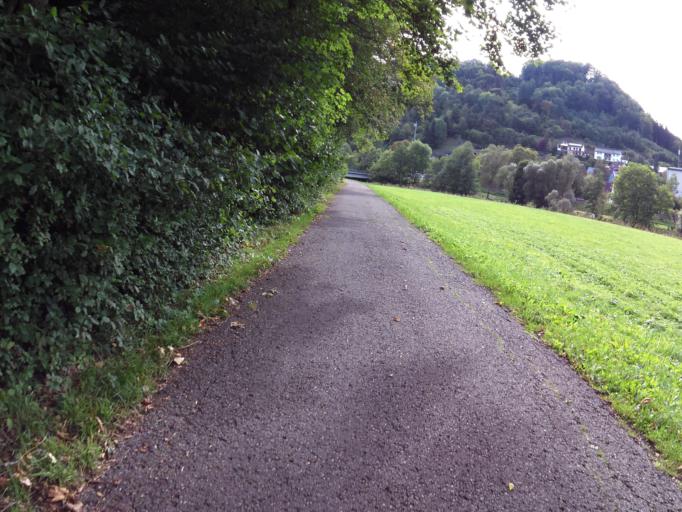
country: DE
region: Baden-Wuerttemberg
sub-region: Freiburg Region
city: Epfendorf
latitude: 48.2240
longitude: 8.6005
